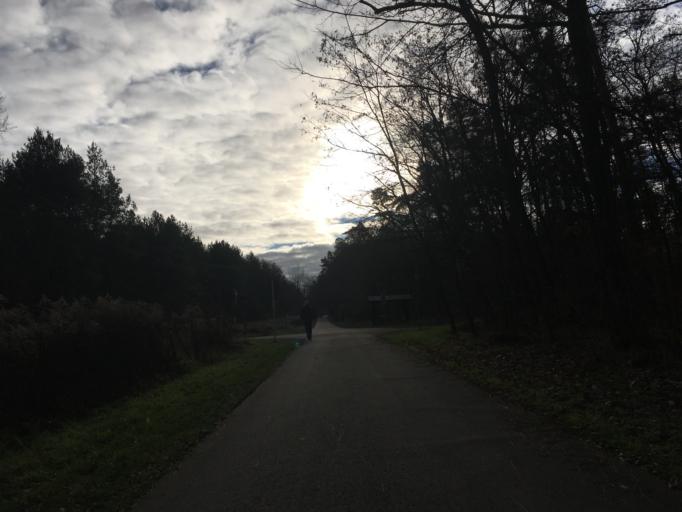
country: DE
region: Brandenburg
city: Waldsieversdorf
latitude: 52.5499
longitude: 14.0833
